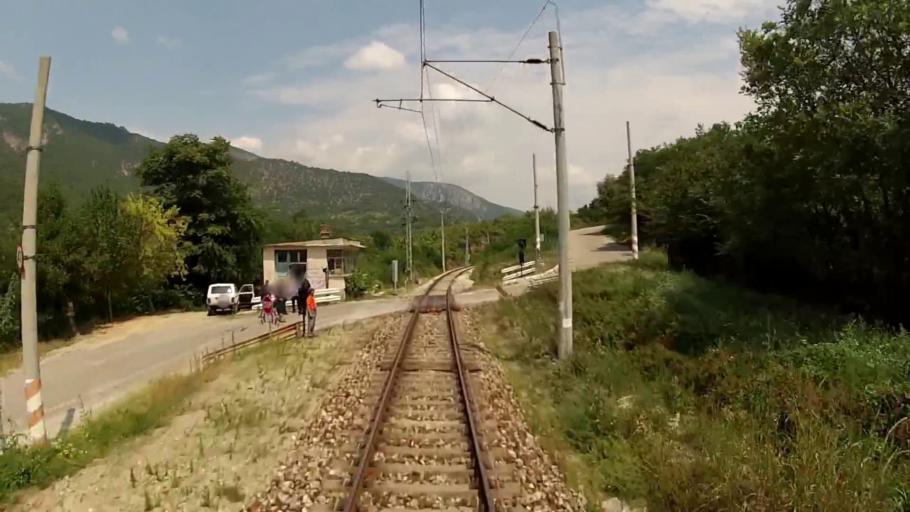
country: BG
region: Blagoevgrad
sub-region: Obshtina Kresna
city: Kresna
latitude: 41.7488
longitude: 23.1561
